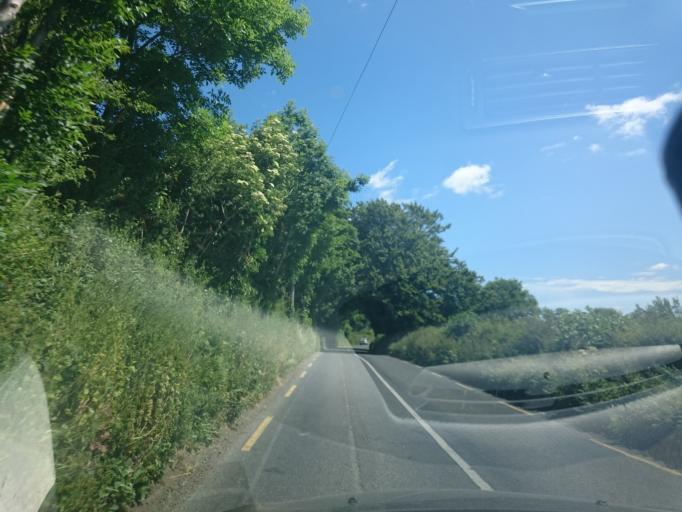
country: IE
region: Leinster
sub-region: County Carlow
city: Bagenalstown
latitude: 52.6292
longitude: -7.0174
